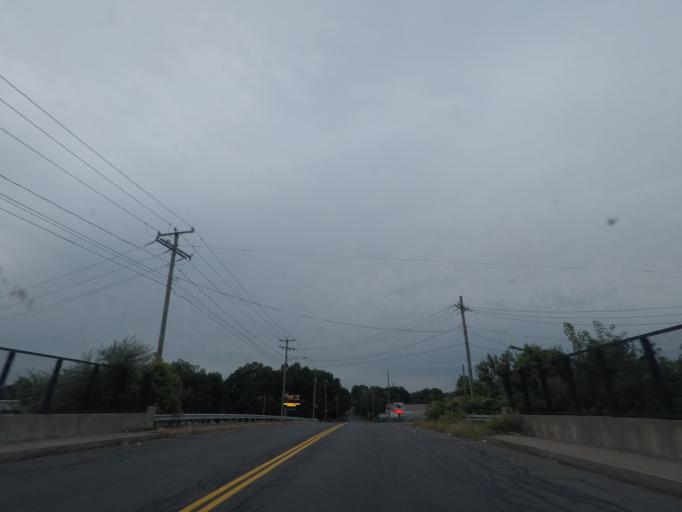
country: US
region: Massachusetts
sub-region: Hampden County
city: Ludlow
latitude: 42.1453
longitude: -72.5032
